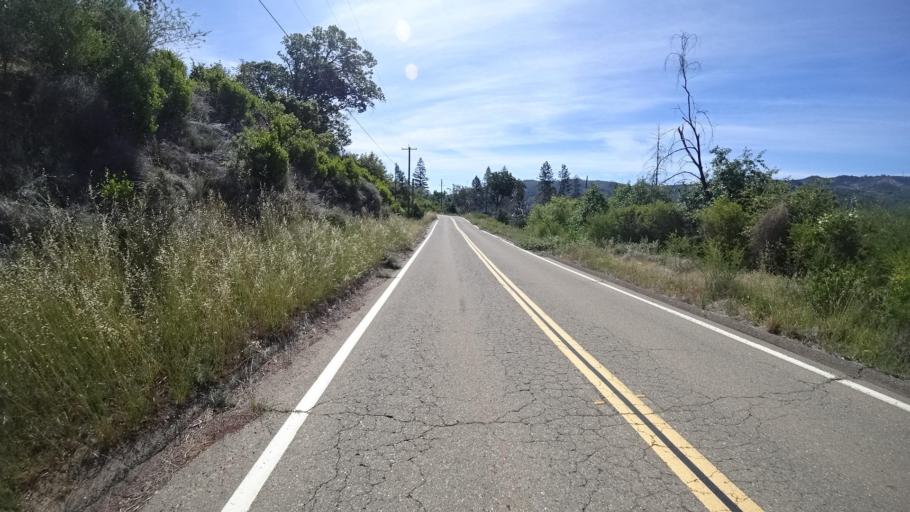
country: US
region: California
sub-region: Lake County
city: Cobb
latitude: 38.7843
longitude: -122.7096
